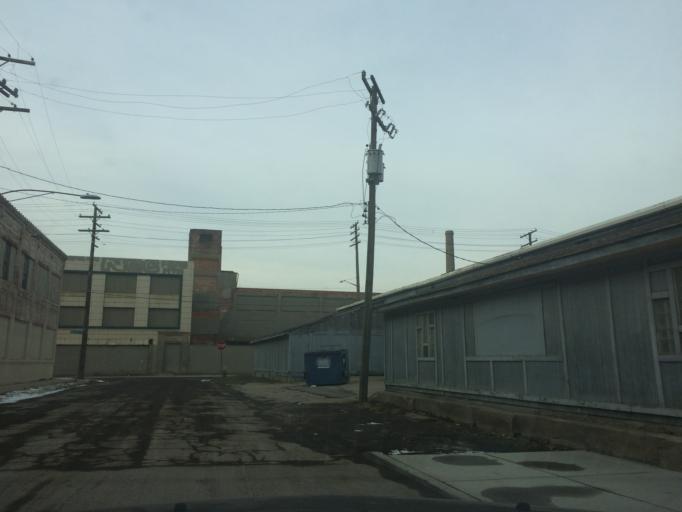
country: US
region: Michigan
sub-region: Wayne County
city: Hamtramck
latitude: 42.3748
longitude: -83.0555
